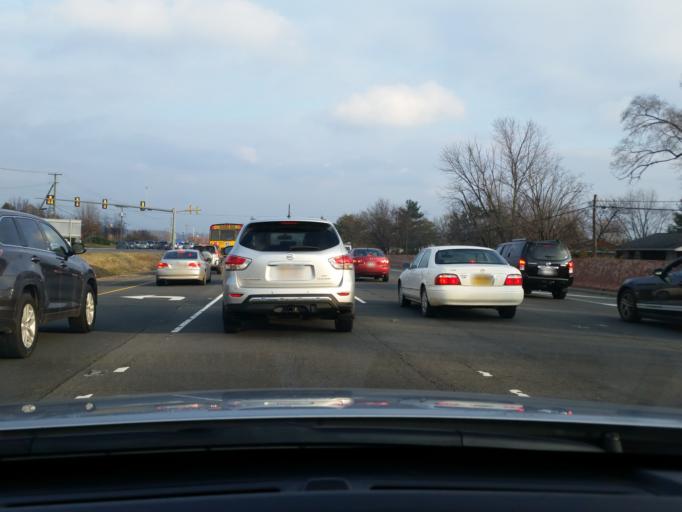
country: US
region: Virginia
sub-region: Loudoun County
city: Sugarland Run
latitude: 39.0199
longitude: -77.3820
